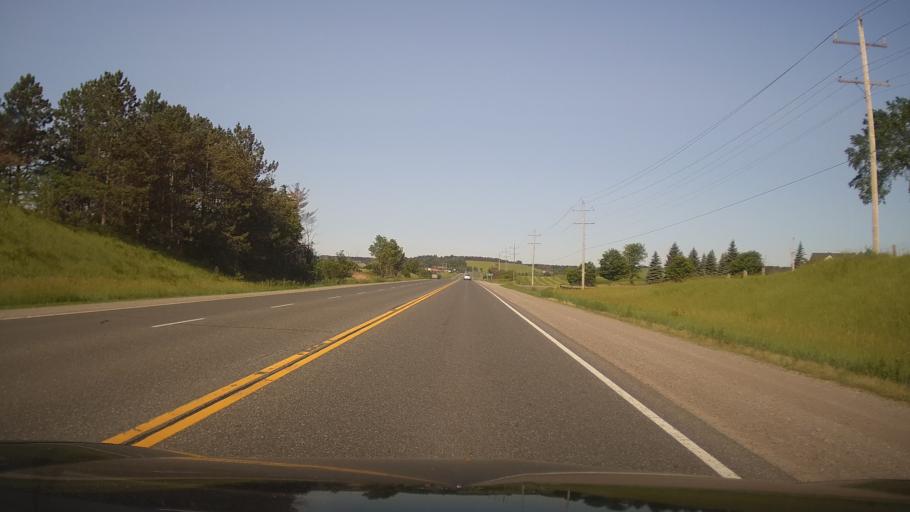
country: CA
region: Ontario
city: Peterborough
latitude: 44.3514
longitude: -78.0619
